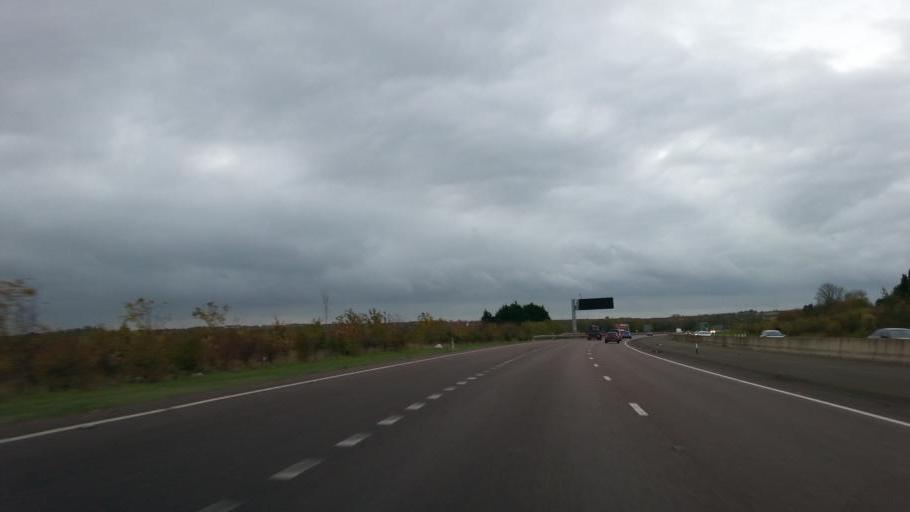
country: GB
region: England
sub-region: Nottinghamshire
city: Bingham
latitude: 52.9623
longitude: -0.9653
